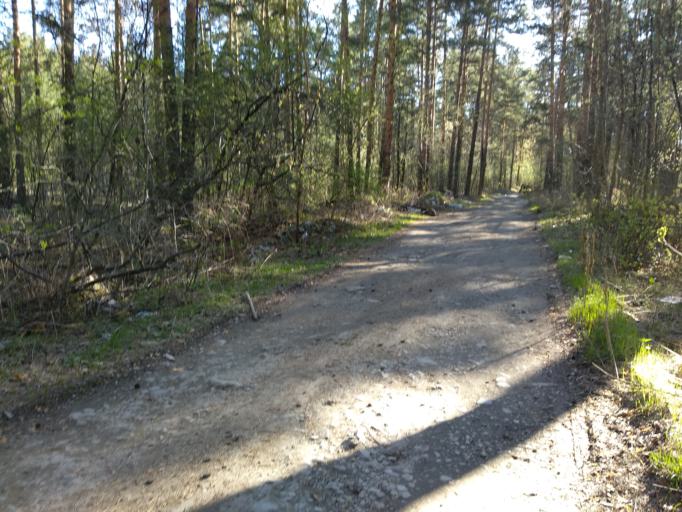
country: RU
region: Sverdlovsk
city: Beryozovsky
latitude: 56.9059
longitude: 60.7532
